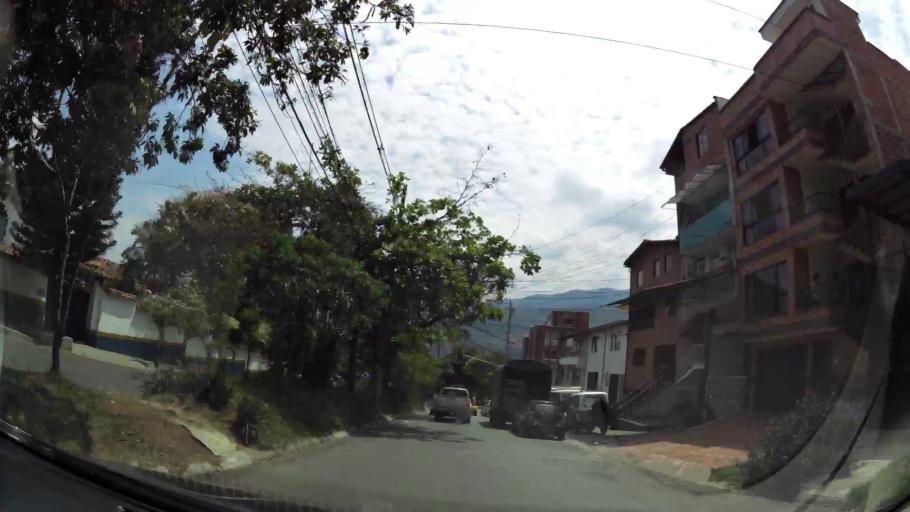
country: CO
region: Antioquia
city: Bello
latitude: 6.3170
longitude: -75.5641
